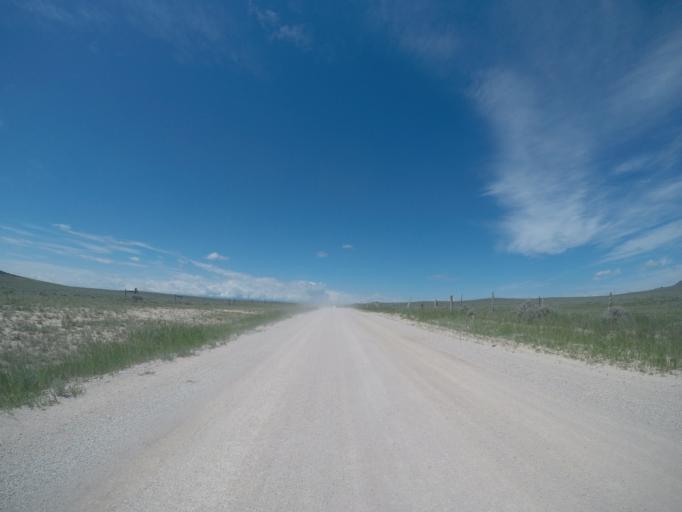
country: US
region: Wyoming
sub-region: Park County
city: Powell
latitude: 45.2050
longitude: -108.7389
